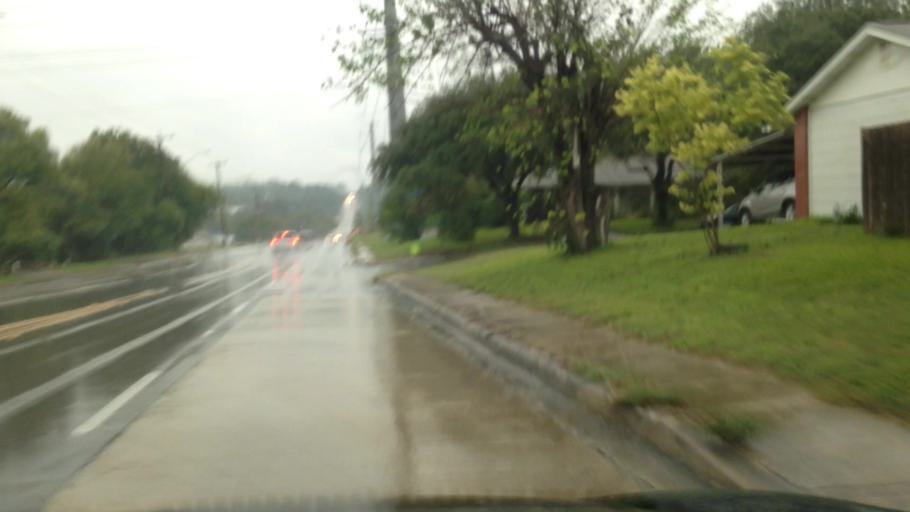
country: US
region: Texas
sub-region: Bexar County
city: Balcones Heights
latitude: 29.5150
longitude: -98.5487
